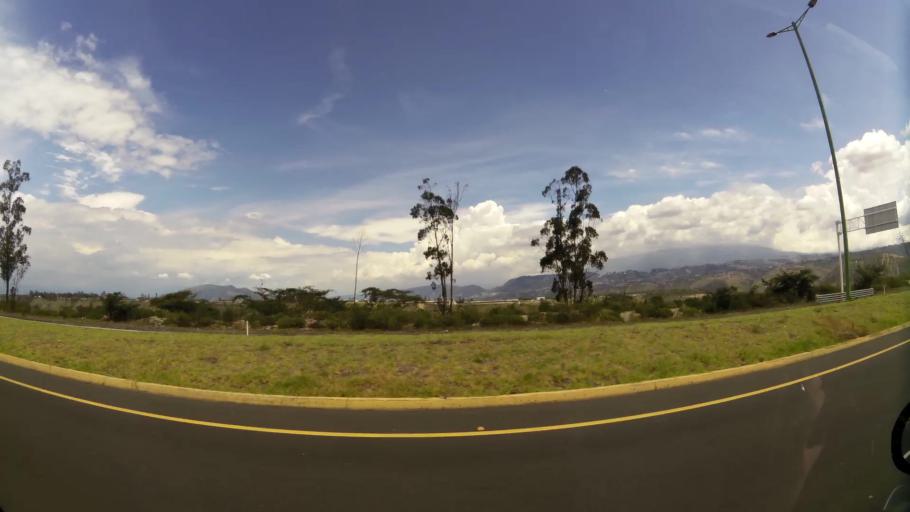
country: EC
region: Pichincha
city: Quito
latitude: -0.1272
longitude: -78.3635
